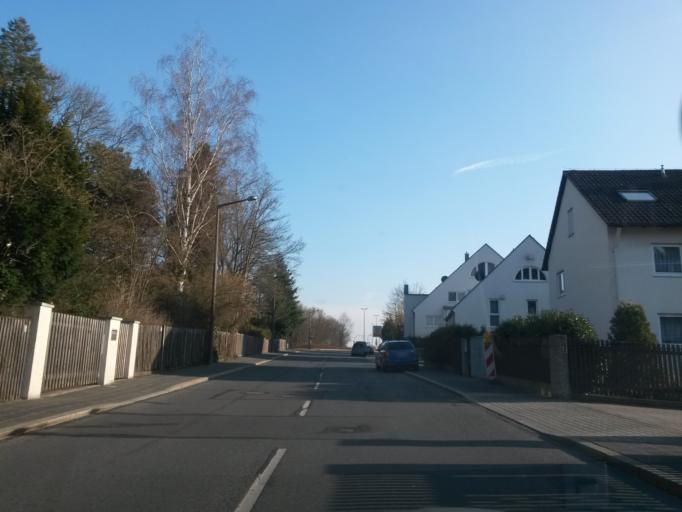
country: DE
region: Bavaria
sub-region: Regierungsbezirk Mittelfranken
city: Furth
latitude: 49.4583
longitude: 10.9749
